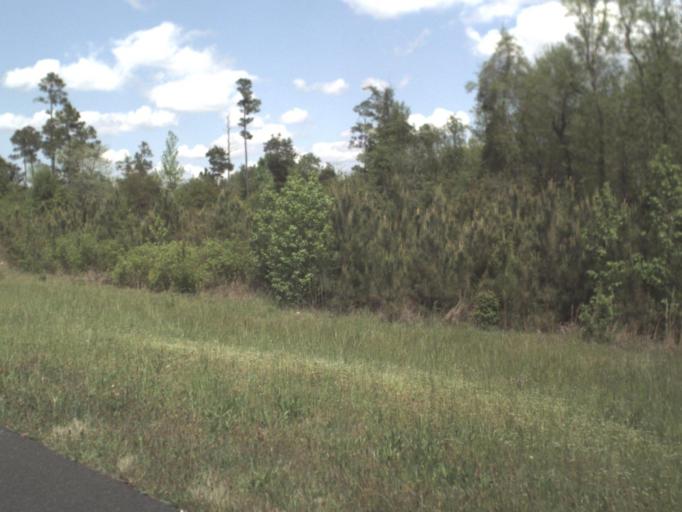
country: US
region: Florida
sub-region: Escambia County
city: Molino
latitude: 30.8451
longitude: -87.3231
